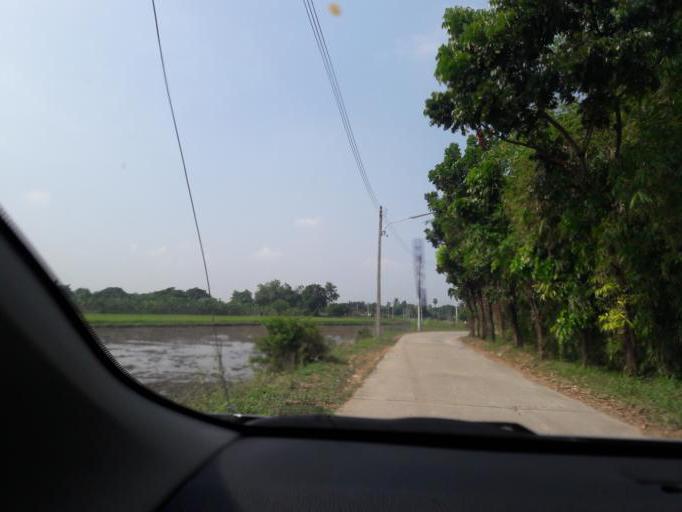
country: TH
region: Ang Thong
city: Ang Thong
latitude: 14.5493
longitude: 100.4305
